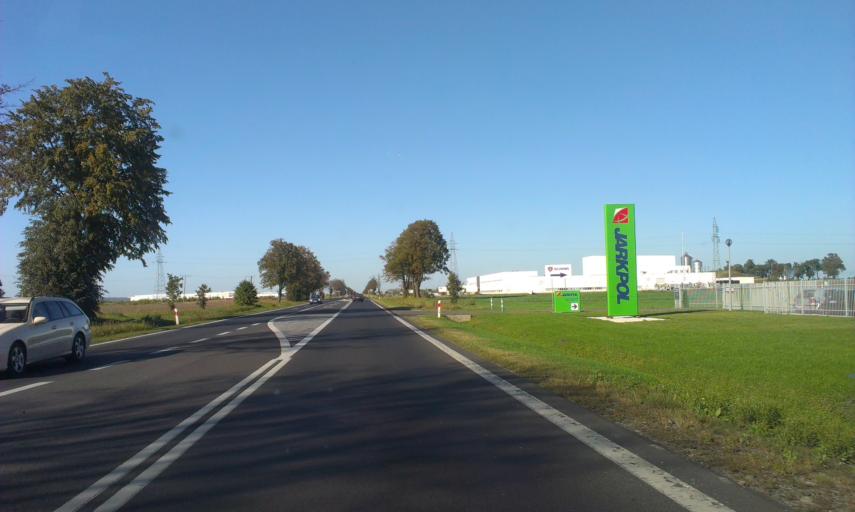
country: PL
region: Kujawsko-Pomorskie
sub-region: Powiat torunski
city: Lysomice
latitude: 53.0958
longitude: 18.6217
